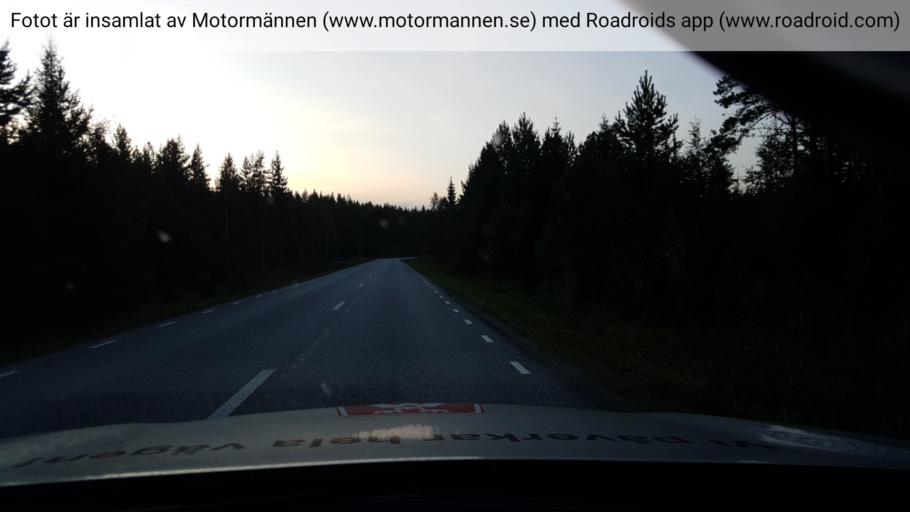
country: SE
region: OErebro
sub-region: Ljusnarsbergs Kommun
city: Kopparberg
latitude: 59.8955
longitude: 15.1025
